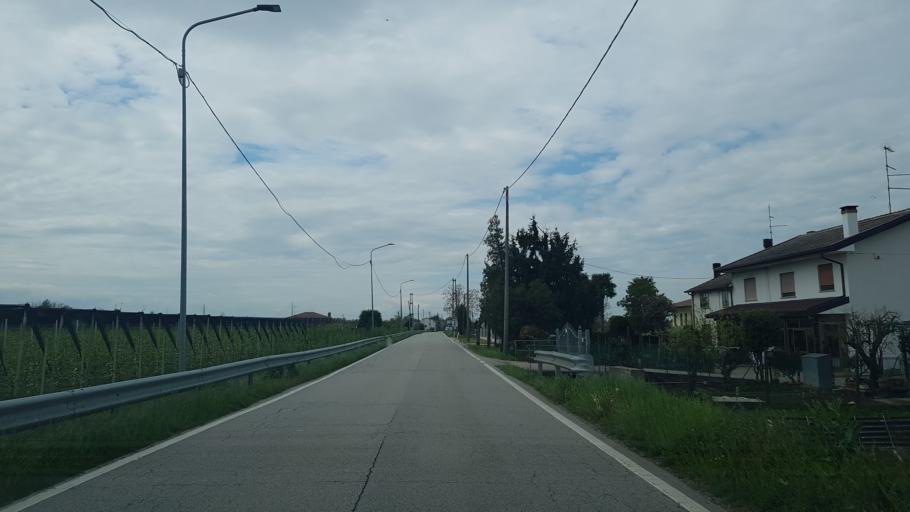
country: IT
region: Veneto
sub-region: Provincia di Padova
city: Piacenza d'Adige
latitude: 45.1252
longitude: 11.5628
